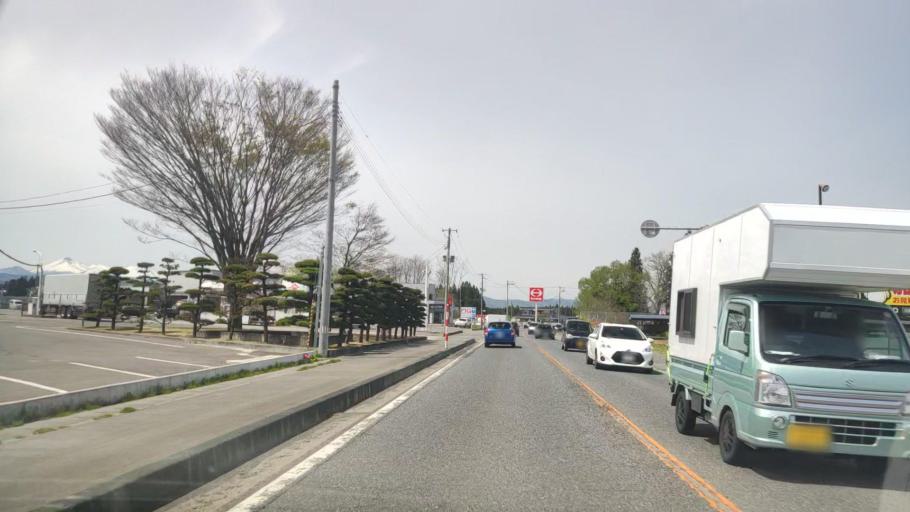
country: JP
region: Aomori
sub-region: Misawa Shi
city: Inuotose
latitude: 40.6736
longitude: 141.1791
